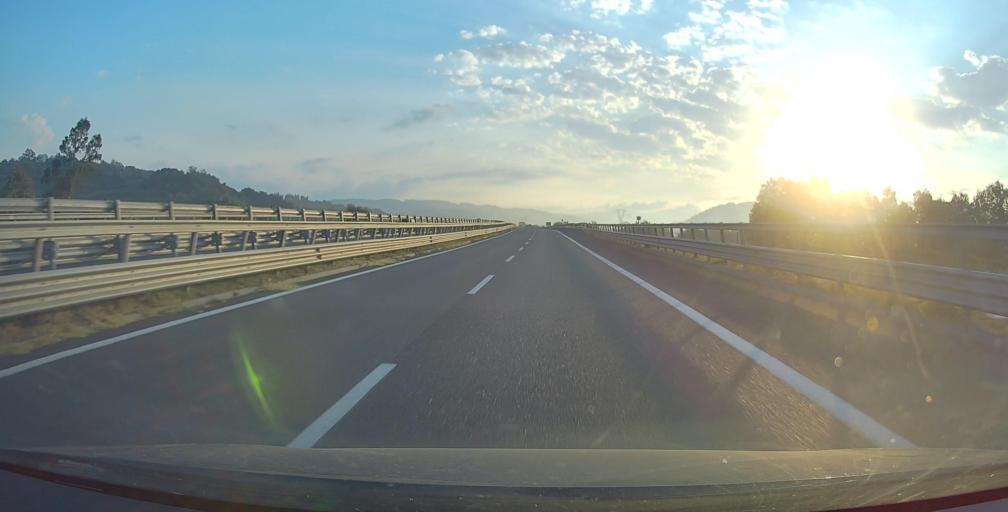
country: IT
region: Calabria
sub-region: Provincia di Reggio Calabria
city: Candidoni
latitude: 38.5078
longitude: 16.0416
